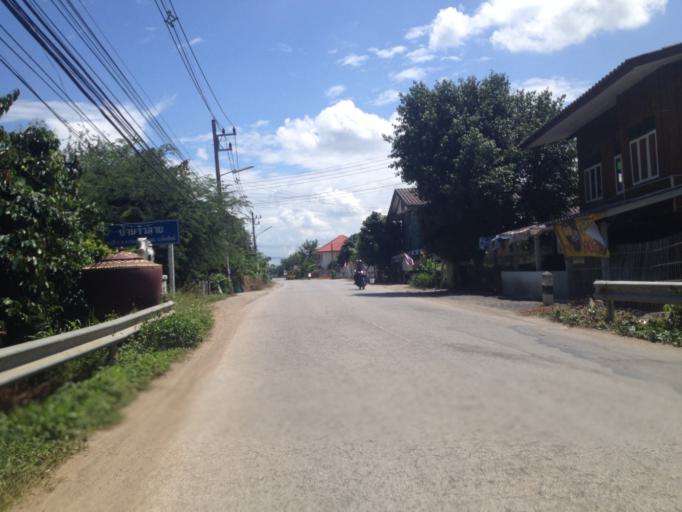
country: TH
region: Chiang Mai
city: San Pa Tong
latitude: 18.6383
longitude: 98.9303
